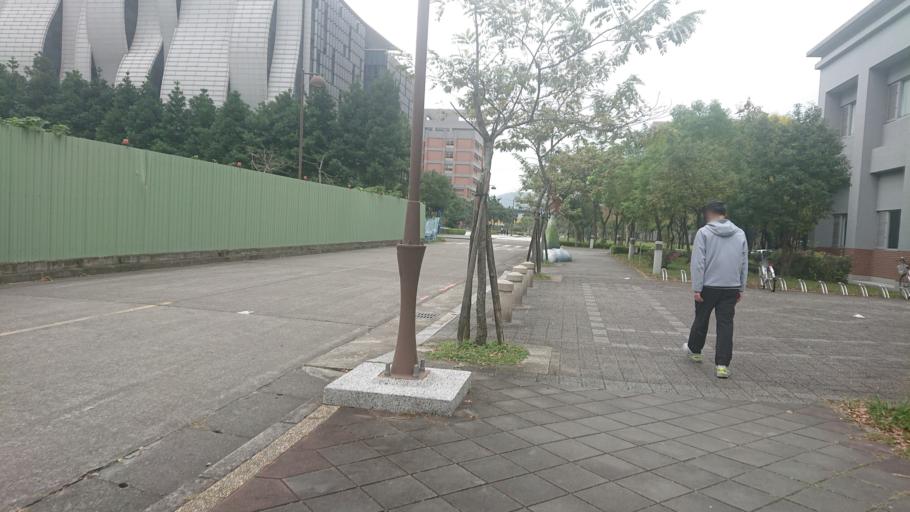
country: TW
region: Taiwan
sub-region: Taoyuan
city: Taoyuan
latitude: 24.9432
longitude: 121.3712
